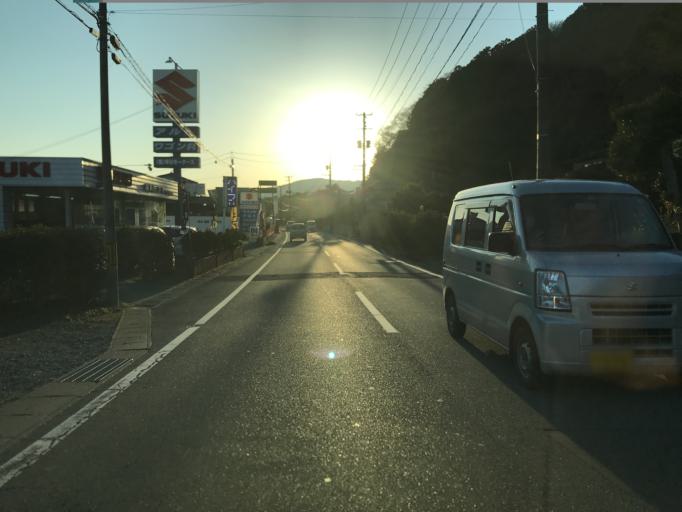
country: JP
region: Fukushima
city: Iwaki
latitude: 37.0548
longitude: 140.8754
